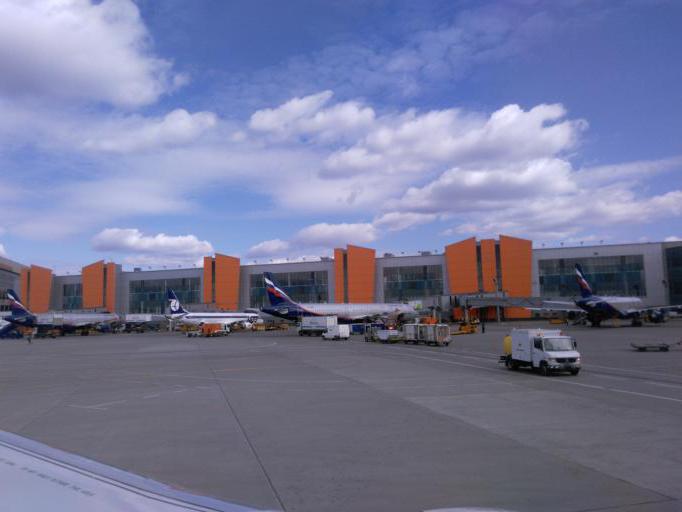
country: RU
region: Moskovskaya
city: Novopodrezkovo
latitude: 55.9648
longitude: 37.4100
